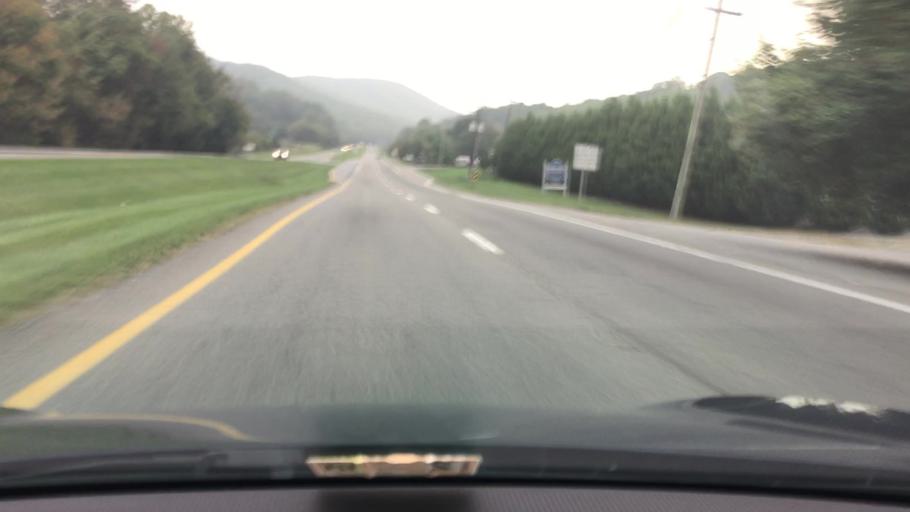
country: US
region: Virginia
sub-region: Botetourt County
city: Blue Ridge
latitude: 37.3862
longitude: -79.7957
